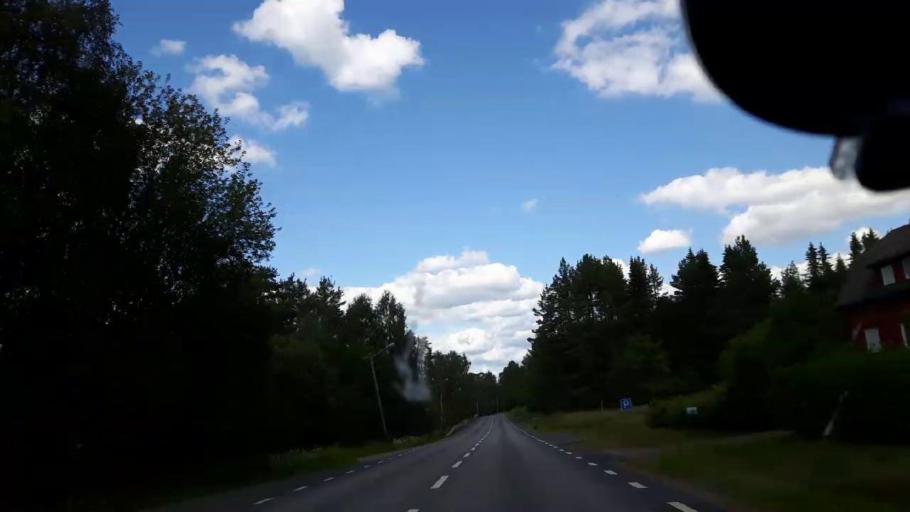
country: SE
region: Jaemtland
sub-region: Ragunda Kommun
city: Hammarstrand
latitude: 63.0002
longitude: 16.6761
